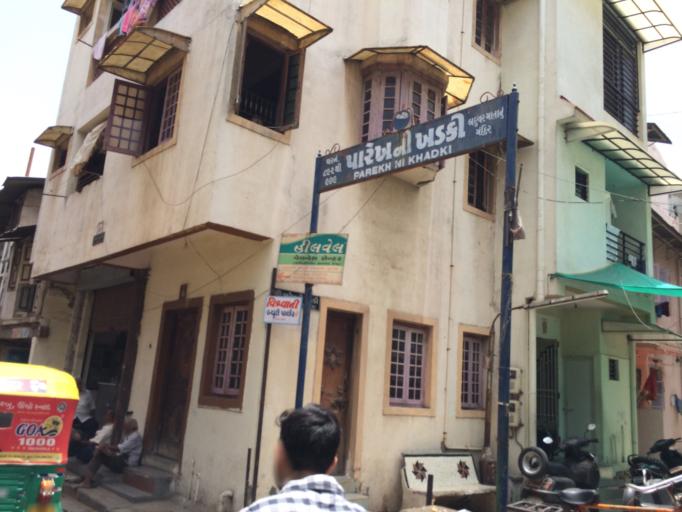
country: IN
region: Gujarat
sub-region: Ahmadabad
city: Ahmedabad
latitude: 23.0210
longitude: 72.5930
